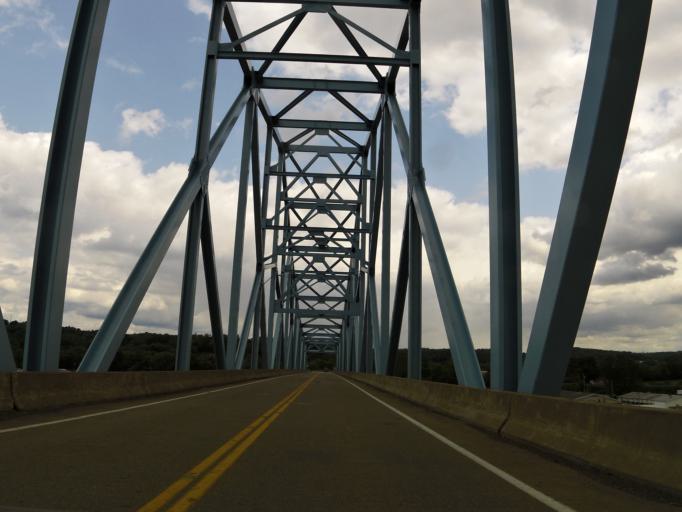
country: US
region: West Virginia
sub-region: Jackson County
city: Ravenswood
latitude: 38.9367
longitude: -81.7560
